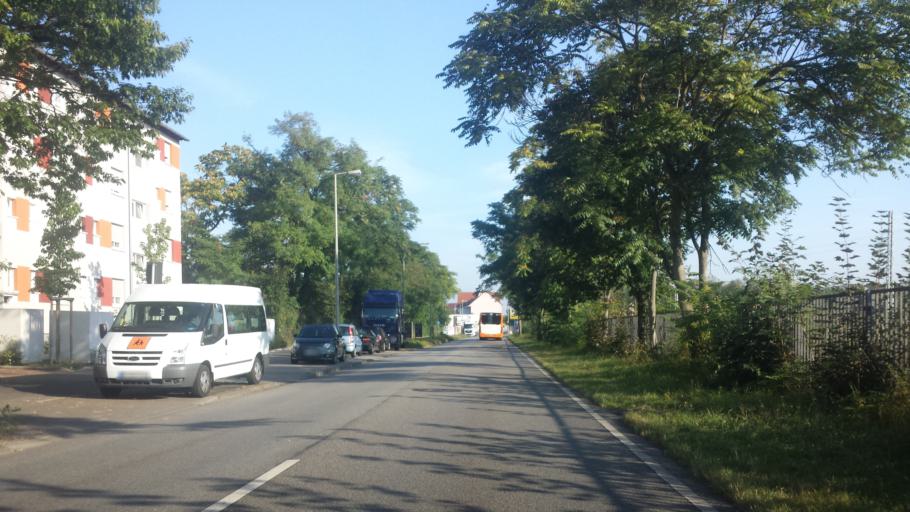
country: DE
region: Baden-Wuerttemberg
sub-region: Karlsruhe Region
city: Mannheim
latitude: 49.5451
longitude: 8.4809
